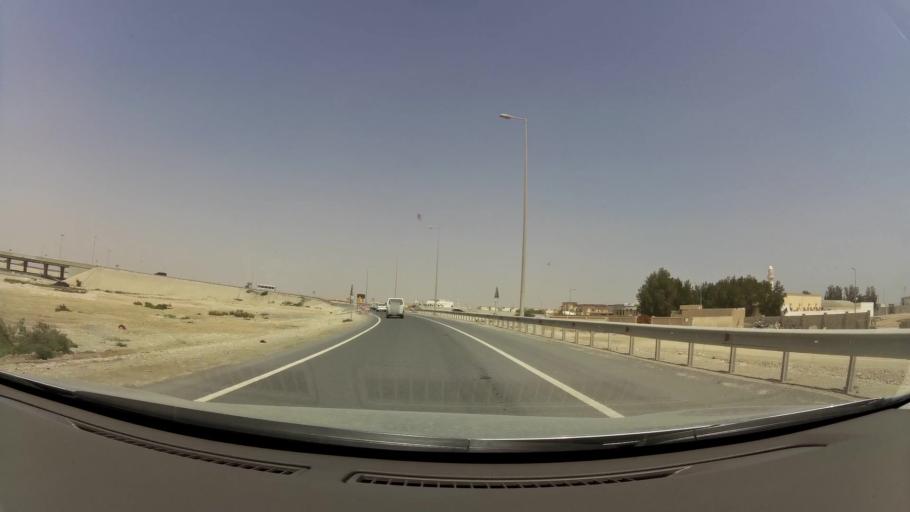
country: QA
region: Baladiyat Umm Salal
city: Umm Salal `Ali
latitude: 25.4847
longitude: 51.4087
